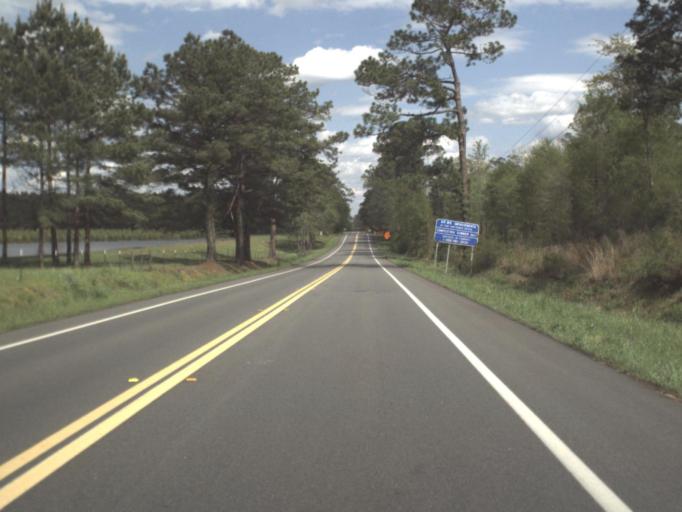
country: US
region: Alabama
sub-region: Covington County
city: Florala
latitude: 30.9666
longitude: -86.3959
